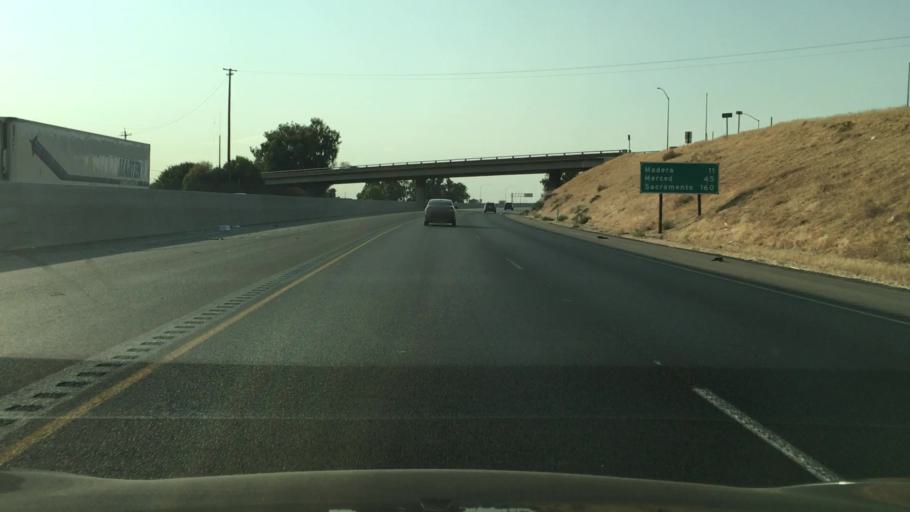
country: US
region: California
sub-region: Fresno County
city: Biola
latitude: 36.8505
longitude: -119.9458
